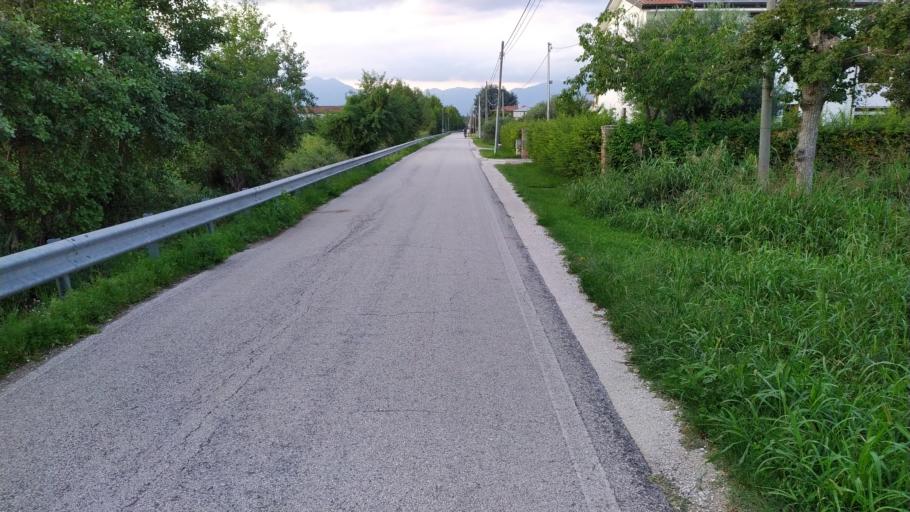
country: IT
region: Veneto
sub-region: Provincia di Vicenza
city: Novoledo
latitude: 45.6382
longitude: 11.5085
